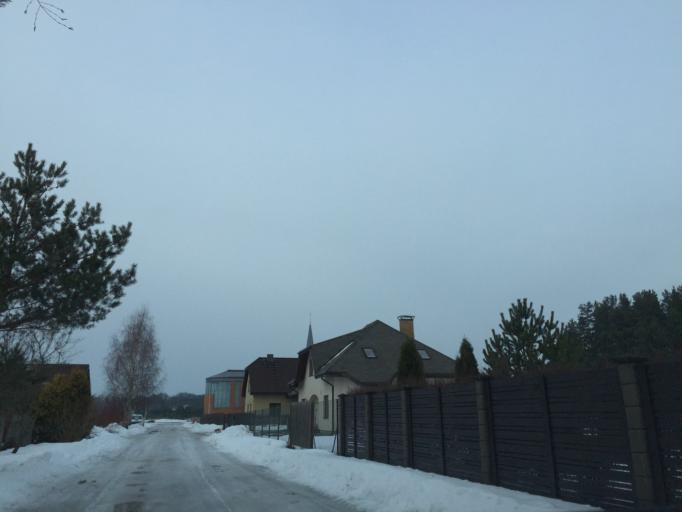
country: LV
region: Ikskile
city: Ikskile
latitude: 56.8400
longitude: 24.4790
